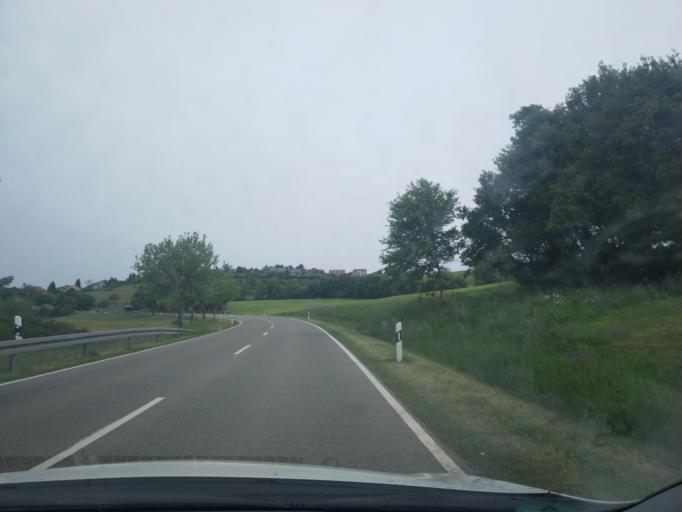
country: DE
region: Baden-Wuerttemberg
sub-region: Freiburg Region
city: Bonndorf im Schwarzwald
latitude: 47.8075
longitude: 8.3466
